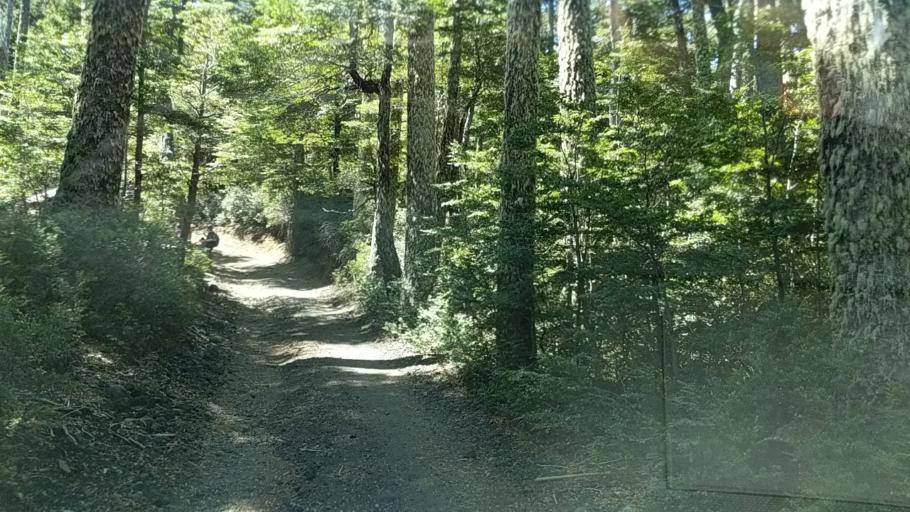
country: CL
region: Araucania
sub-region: Provincia de Cautin
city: Pucon
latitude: -39.4629
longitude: -71.8514
